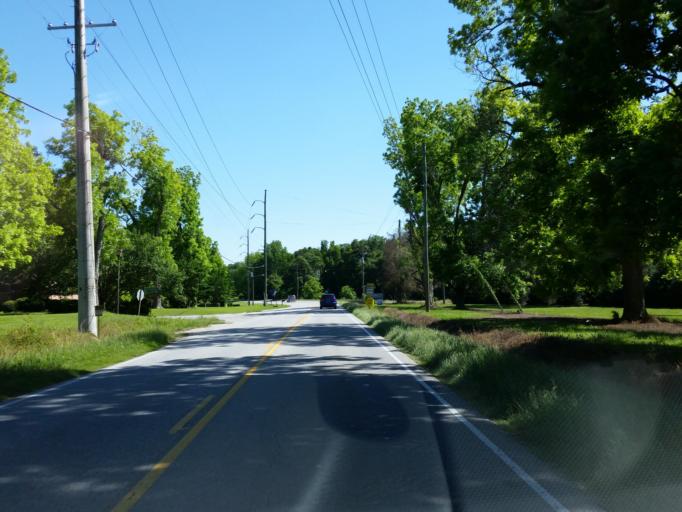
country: US
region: Georgia
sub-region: Lowndes County
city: Hahira
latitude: 30.9254
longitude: -83.3500
